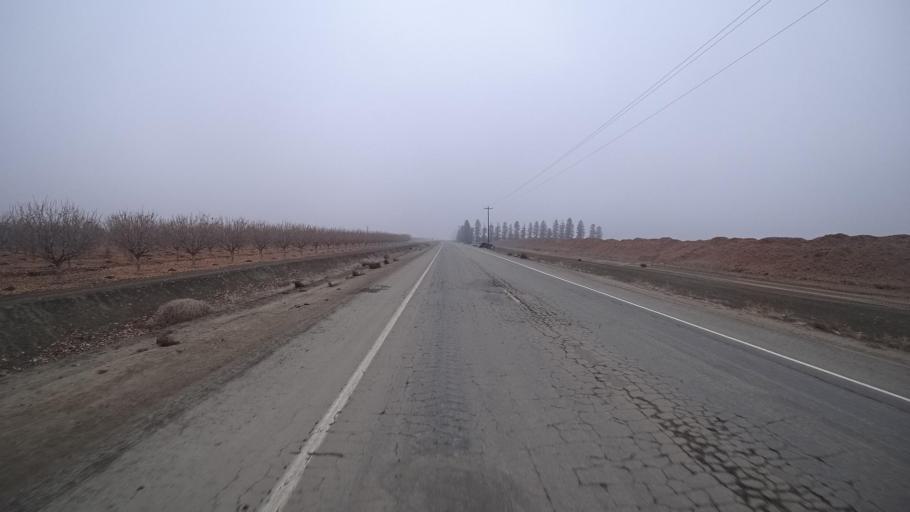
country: US
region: California
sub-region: Kern County
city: Buttonwillow
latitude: 35.4103
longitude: -119.5185
